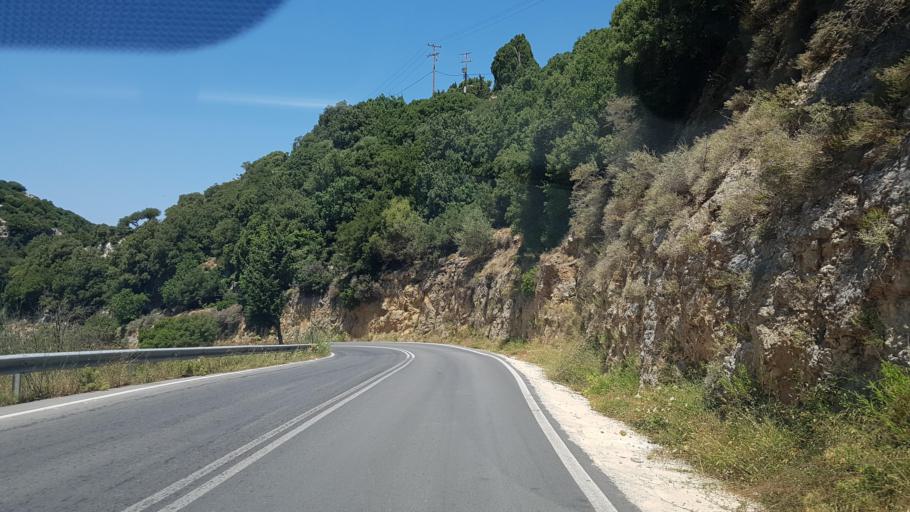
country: GR
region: Crete
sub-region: Nomos Rethymnis
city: Agia Foteini
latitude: 35.3087
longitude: 24.6280
